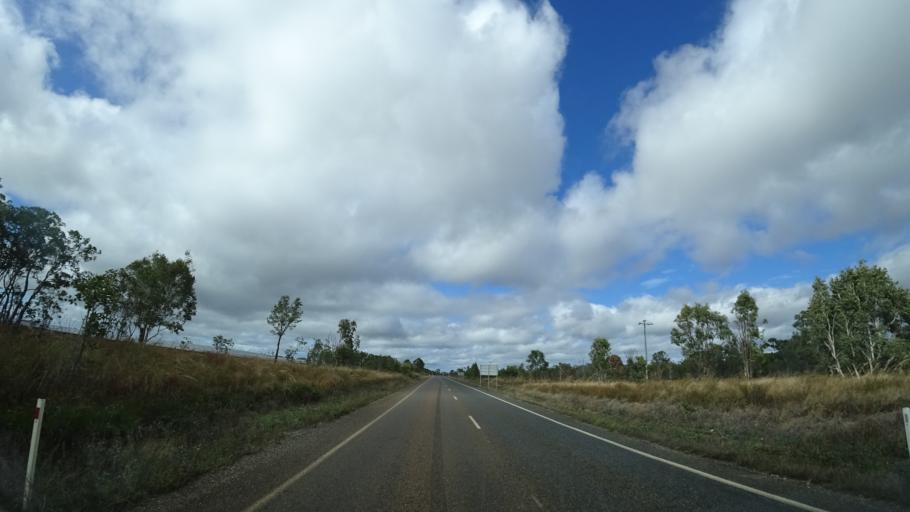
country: AU
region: Queensland
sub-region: Cook
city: Cooktown
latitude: -15.8668
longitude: 144.8592
